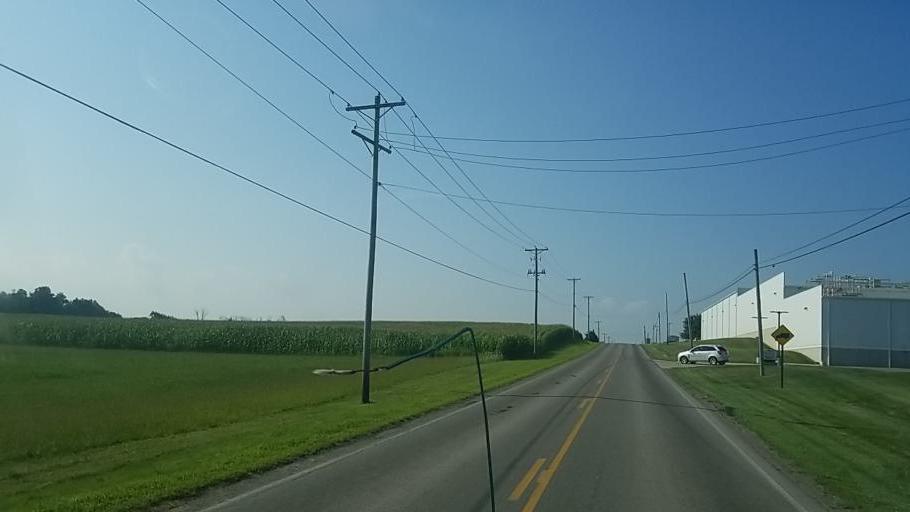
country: US
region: Ohio
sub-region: Wayne County
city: Dalton
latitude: 40.7294
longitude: -81.7450
